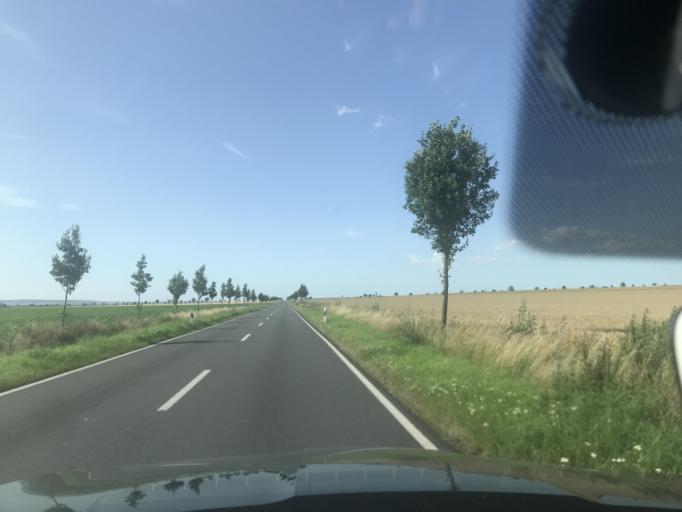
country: DE
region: Saxony-Anhalt
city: Ditfurt
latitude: 51.8395
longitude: 11.1970
